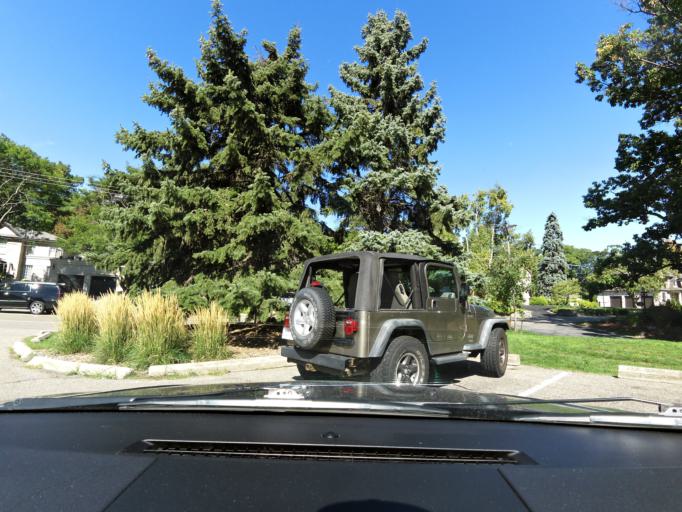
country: CA
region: Ontario
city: Hamilton
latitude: 43.3075
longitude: -79.8316
